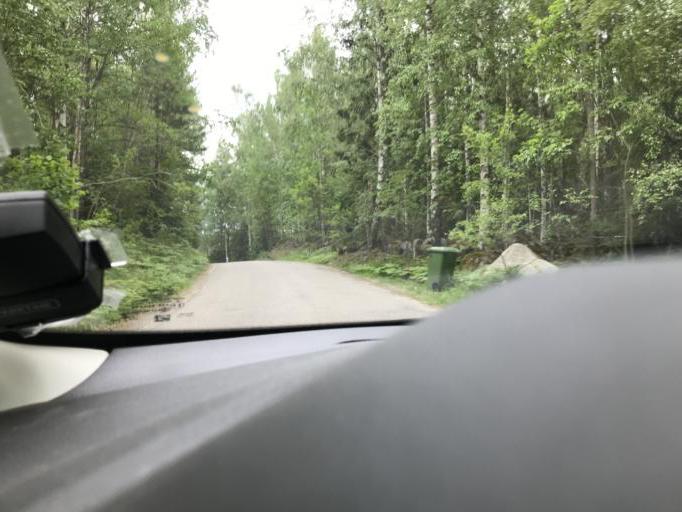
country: SE
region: Stockholm
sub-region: Botkyrka Kommun
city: Varsta
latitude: 59.1940
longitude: 17.7824
